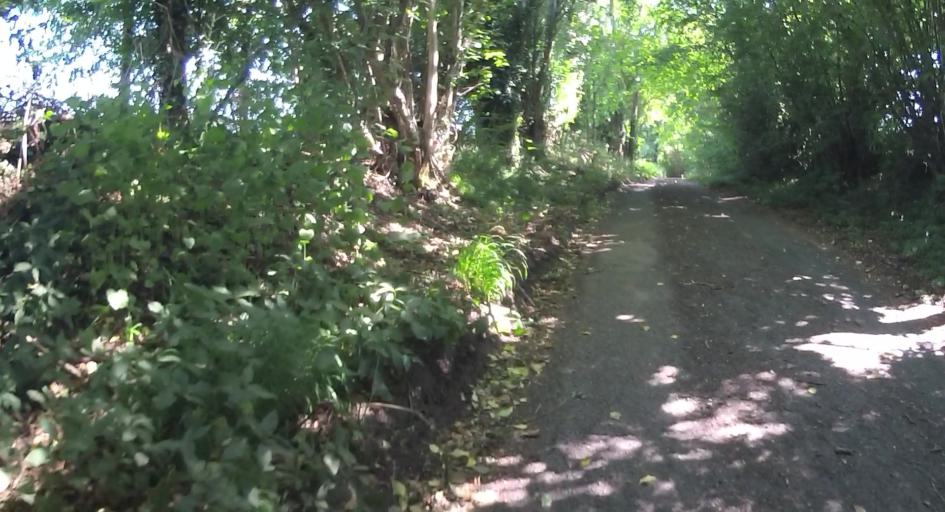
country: GB
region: England
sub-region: Hampshire
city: Kingsclere
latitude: 51.3536
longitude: -1.2743
